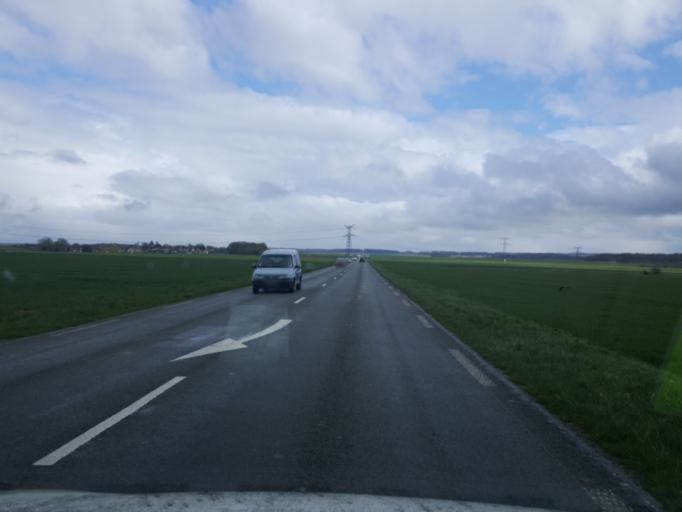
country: FR
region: Picardie
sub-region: Departement de l'Oise
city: Chaumont-en-Vexin
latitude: 49.3120
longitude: 1.8788
